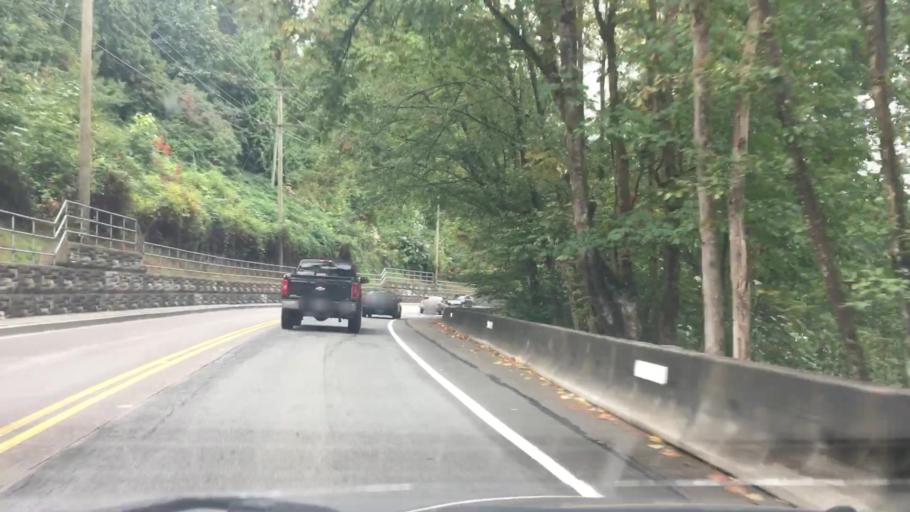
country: CA
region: British Columbia
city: Langley
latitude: 49.1043
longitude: -122.5697
